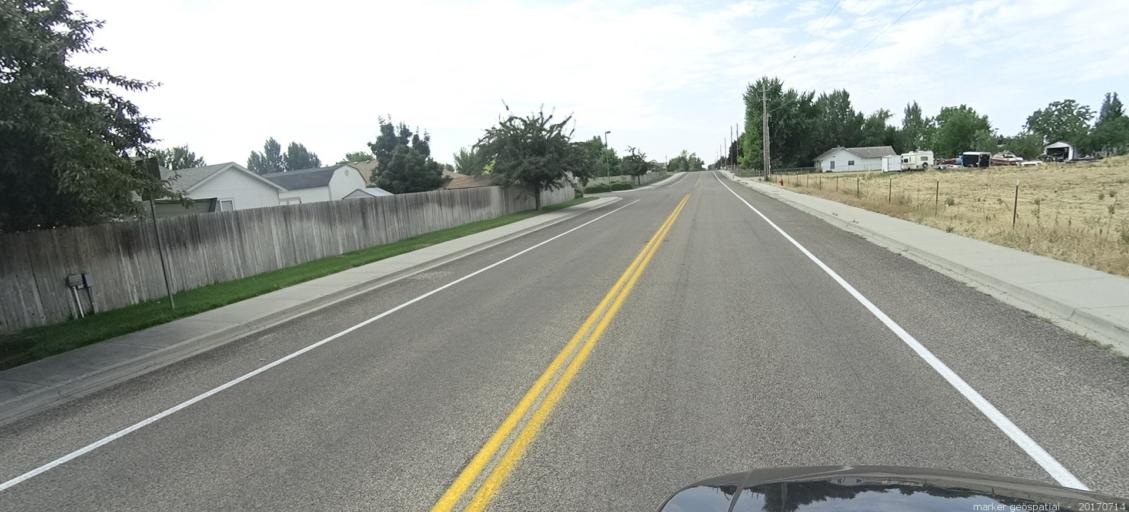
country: US
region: Idaho
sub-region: Ada County
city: Kuna
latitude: 43.5024
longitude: -116.4238
